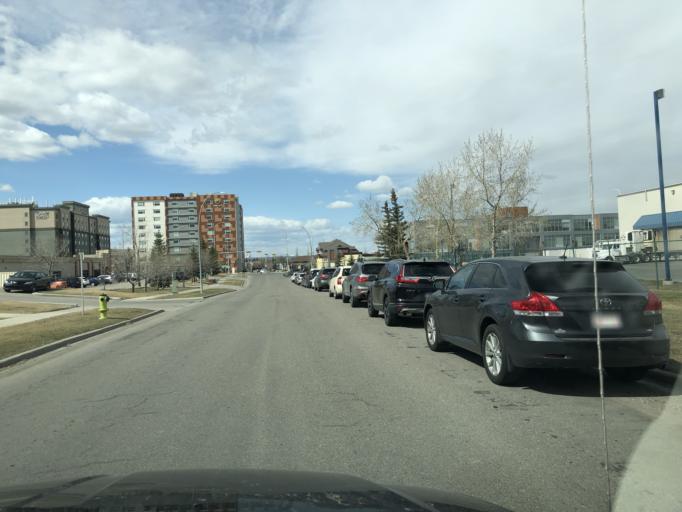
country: CA
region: Alberta
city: Calgary
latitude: 51.0719
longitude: -113.9958
